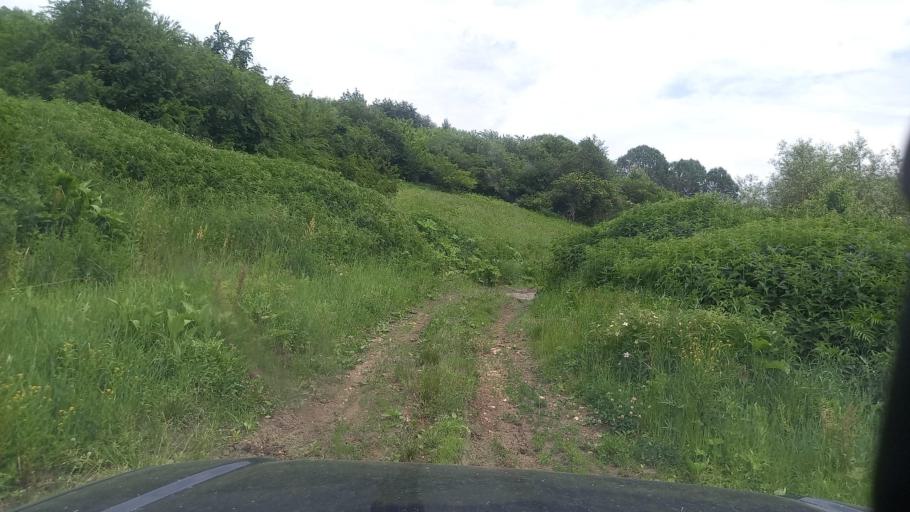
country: RU
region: Karachayevo-Cherkesiya
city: Pregradnaya
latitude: 44.0874
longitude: 41.2030
